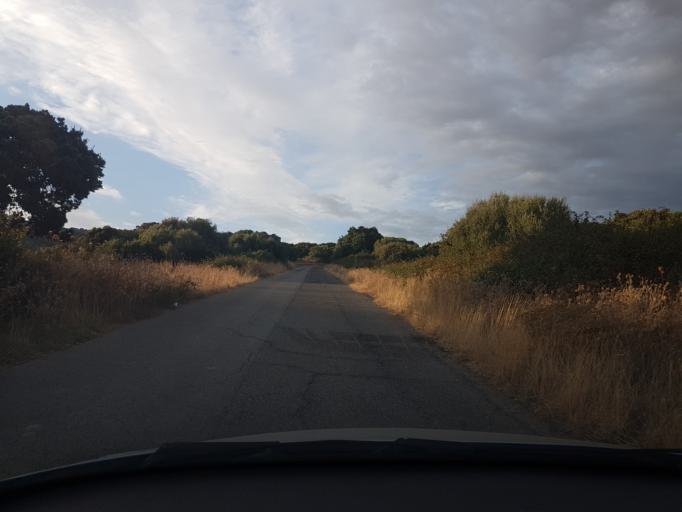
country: IT
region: Sardinia
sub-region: Provincia di Oristano
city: Seneghe
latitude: 40.0997
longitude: 8.6210
